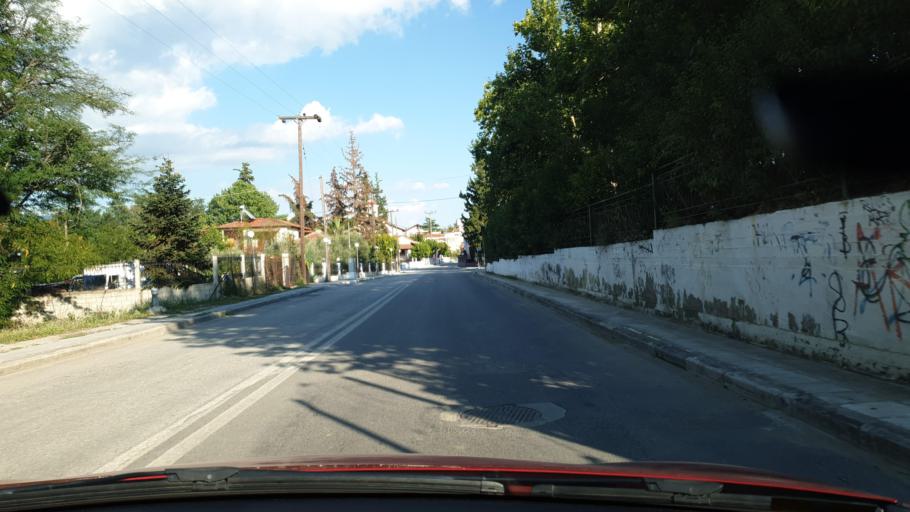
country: GR
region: Central Macedonia
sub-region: Nomos Thessalonikis
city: Souroti
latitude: 40.4739
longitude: 23.0894
